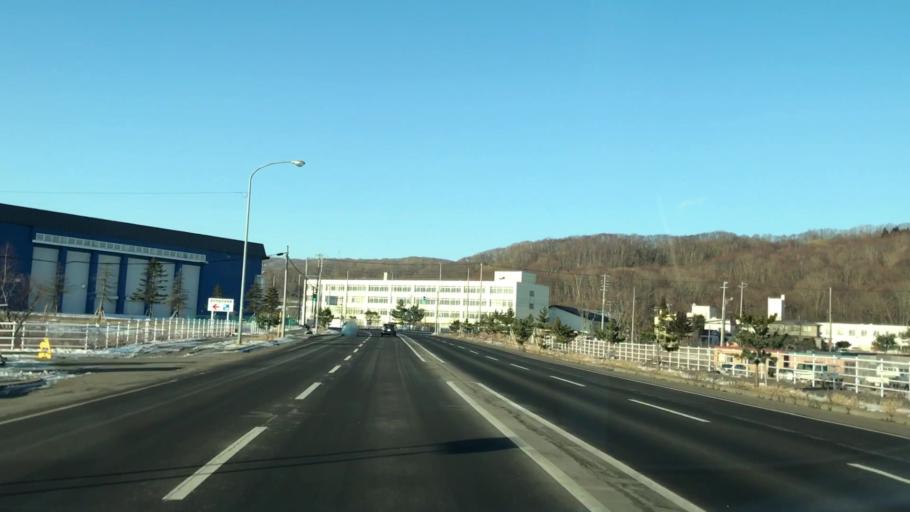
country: JP
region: Hokkaido
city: Muroran
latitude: 42.3928
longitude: 141.0814
